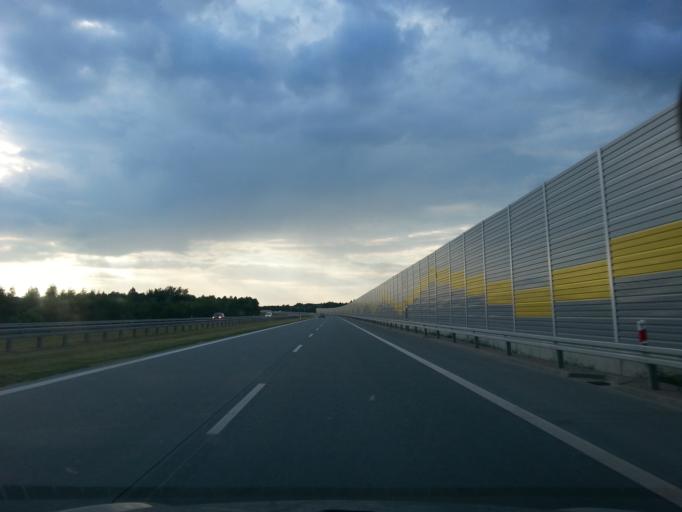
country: PL
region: Lodz Voivodeship
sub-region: Powiat zdunskowolski
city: Zdunska Wola
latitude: 51.5885
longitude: 18.8949
